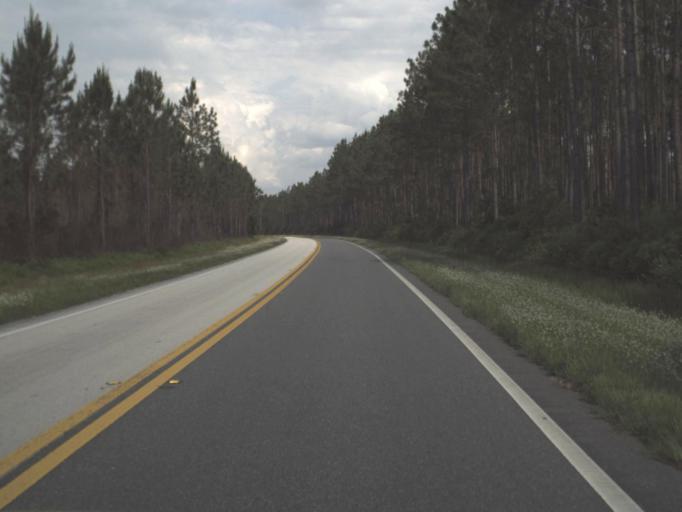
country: US
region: Florida
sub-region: Columbia County
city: Five Points
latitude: 30.5700
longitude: -82.4500
